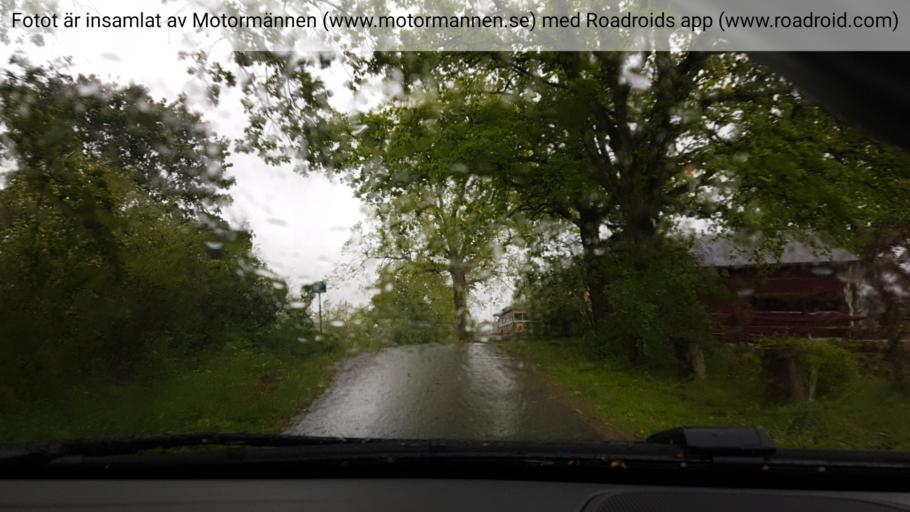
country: SE
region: Stockholm
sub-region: Haninge Kommun
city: Jordbro
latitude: 59.0152
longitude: 18.1141
